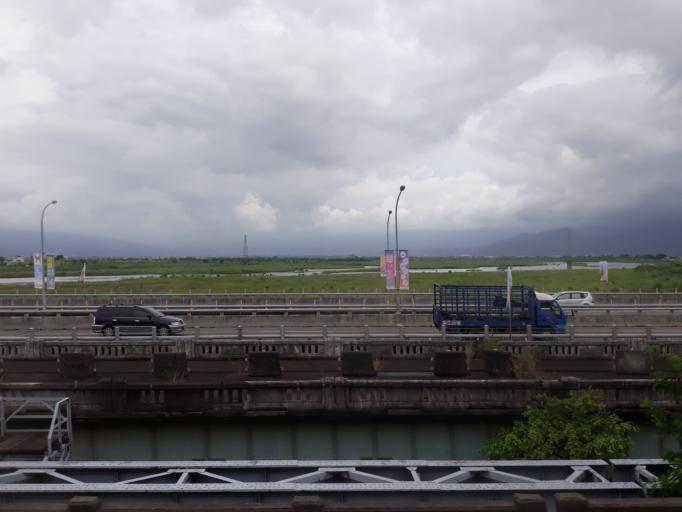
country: TW
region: Taiwan
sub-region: Yilan
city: Yilan
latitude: 24.7168
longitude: 121.7720
